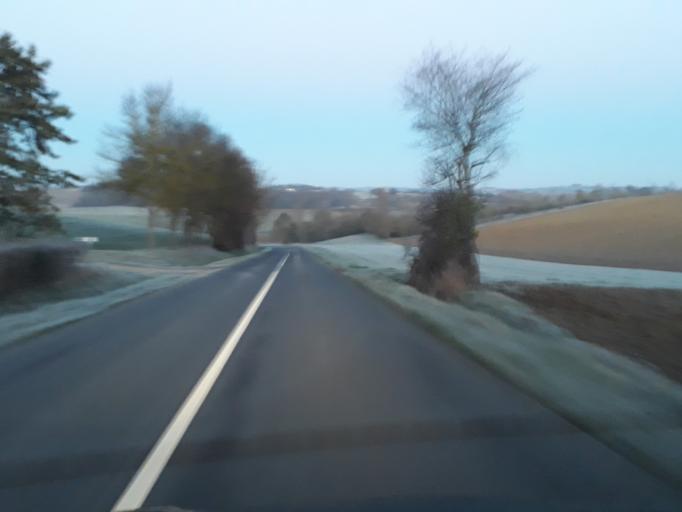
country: FR
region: Midi-Pyrenees
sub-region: Departement du Gers
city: Samatan
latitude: 43.4725
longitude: 0.9632
